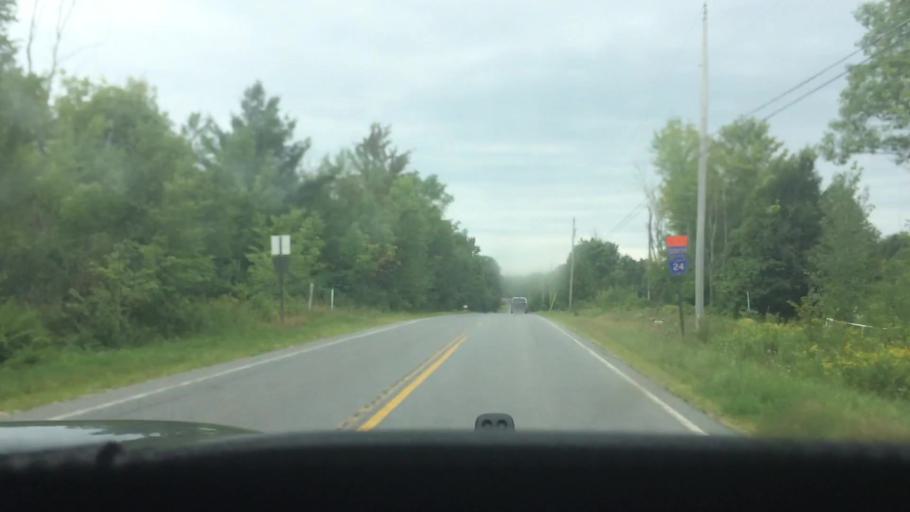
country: US
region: New York
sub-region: St. Lawrence County
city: Canton
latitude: 44.5052
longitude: -75.2132
